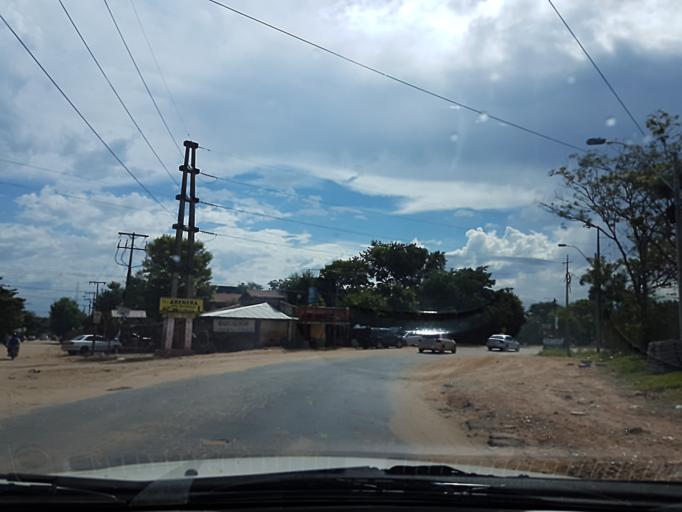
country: PY
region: Asuncion
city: Asuncion
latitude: -25.2450
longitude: -57.5802
